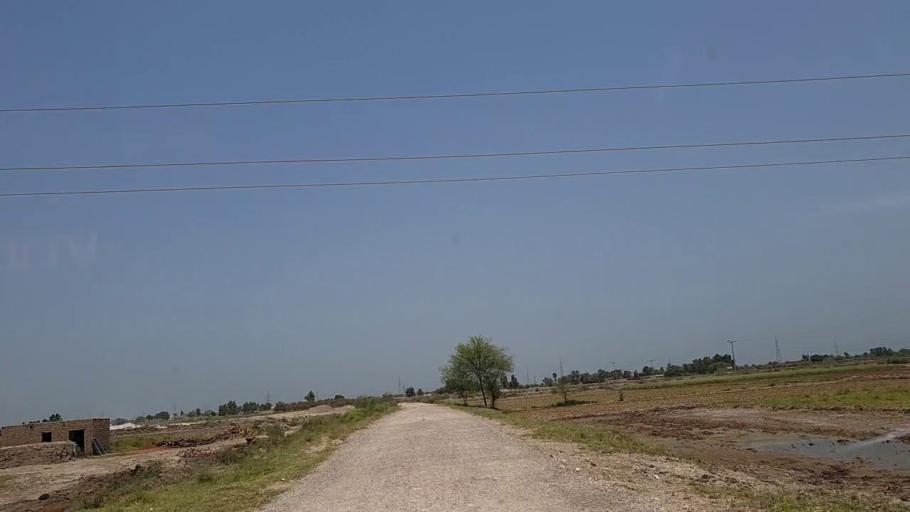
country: PK
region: Sindh
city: Ghotki
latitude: 27.9868
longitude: 69.3674
